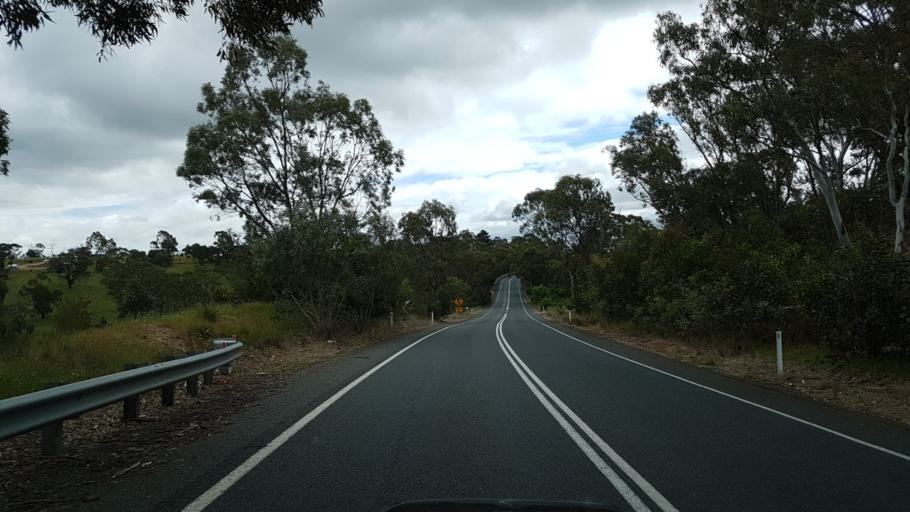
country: AU
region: South Australia
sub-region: Playford
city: One Tree Hill
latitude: -34.7388
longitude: 138.8022
